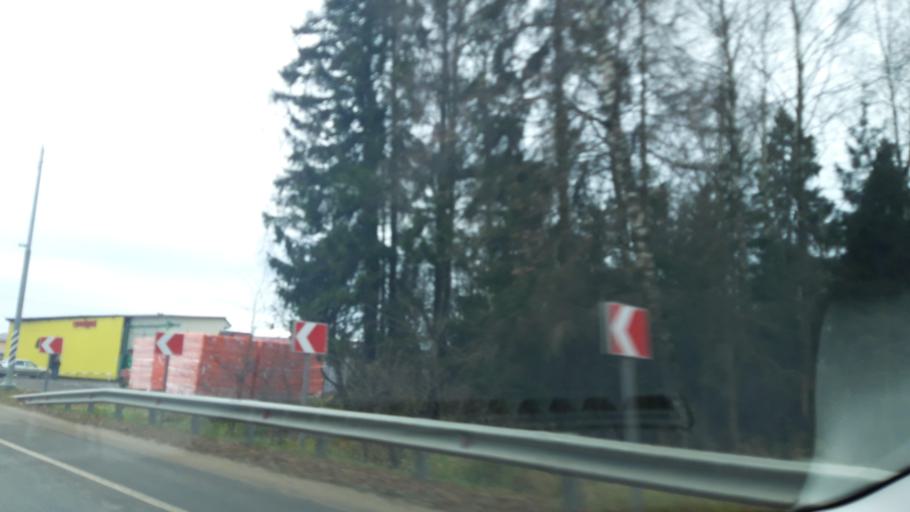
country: RU
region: Moskovskaya
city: Solnechnogorsk
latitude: 56.1393
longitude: 36.9170
